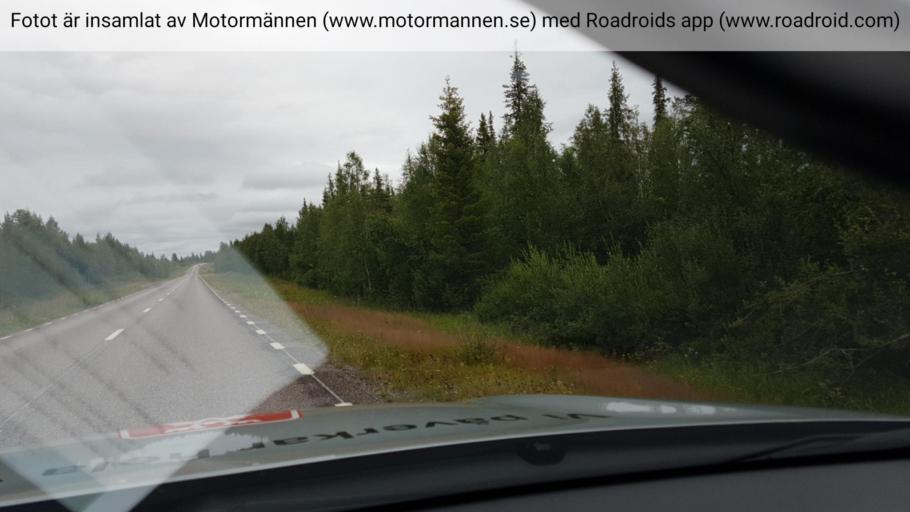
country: SE
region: Norrbotten
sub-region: Gallivare Kommun
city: Gaellivare
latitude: 67.0701
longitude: 21.5082
